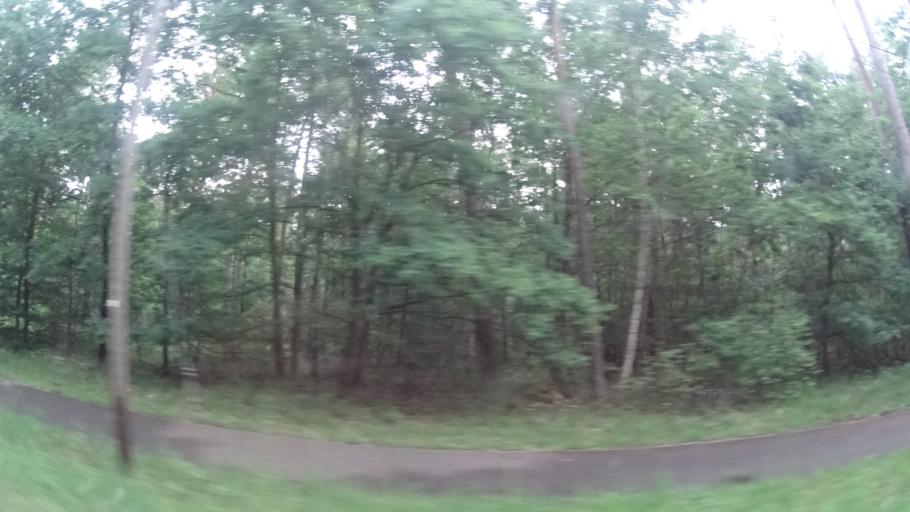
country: DE
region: Rheinland-Pfalz
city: Dudenhofen
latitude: 49.3401
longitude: 8.3758
